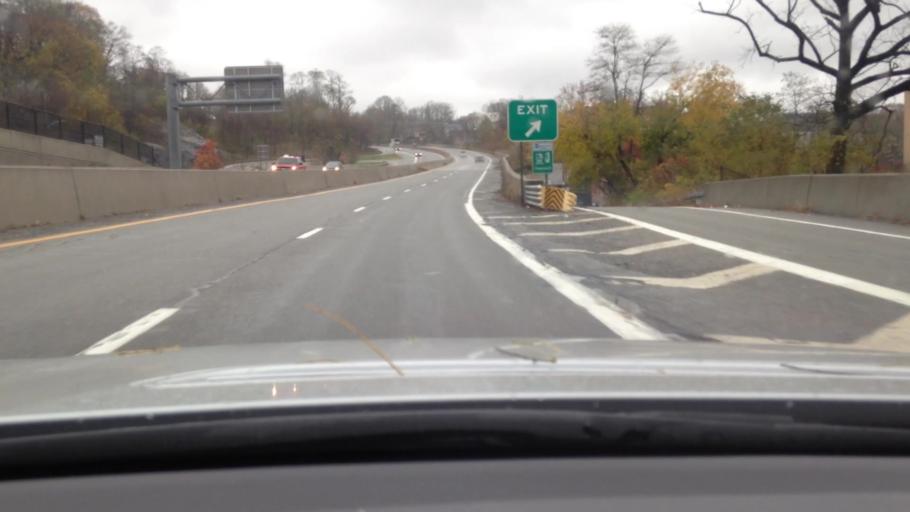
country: US
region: New York
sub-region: Westchester County
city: Peekskill
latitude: 41.2875
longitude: -73.9281
